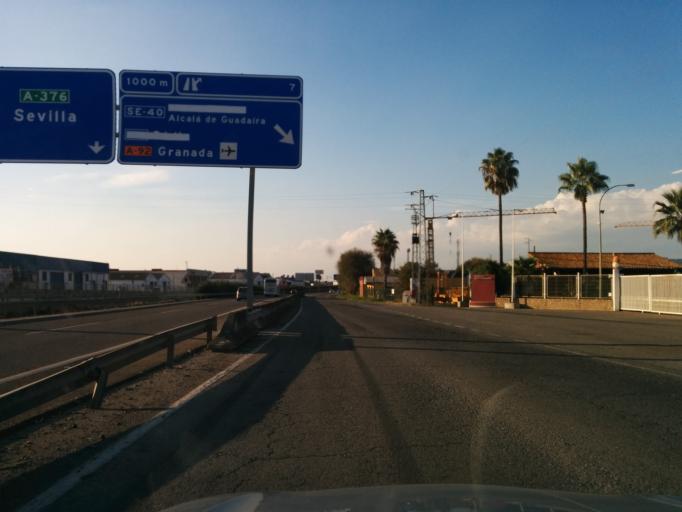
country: ES
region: Andalusia
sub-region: Provincia de Sevilla
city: Dos Hermanas
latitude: 37.3090
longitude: -5.8891
